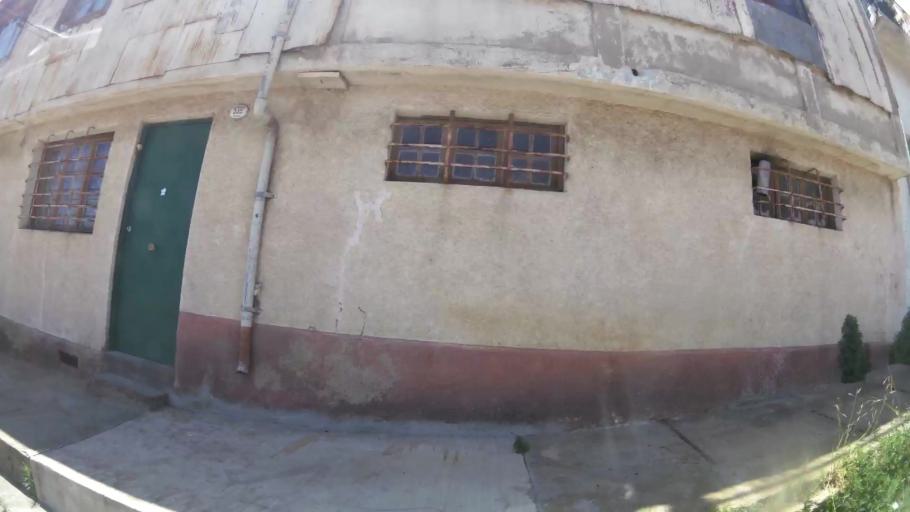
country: CL
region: Valparaiso
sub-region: Provincia de Valparaiso
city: Valparaiso
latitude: -33.0330
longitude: -71.6417
